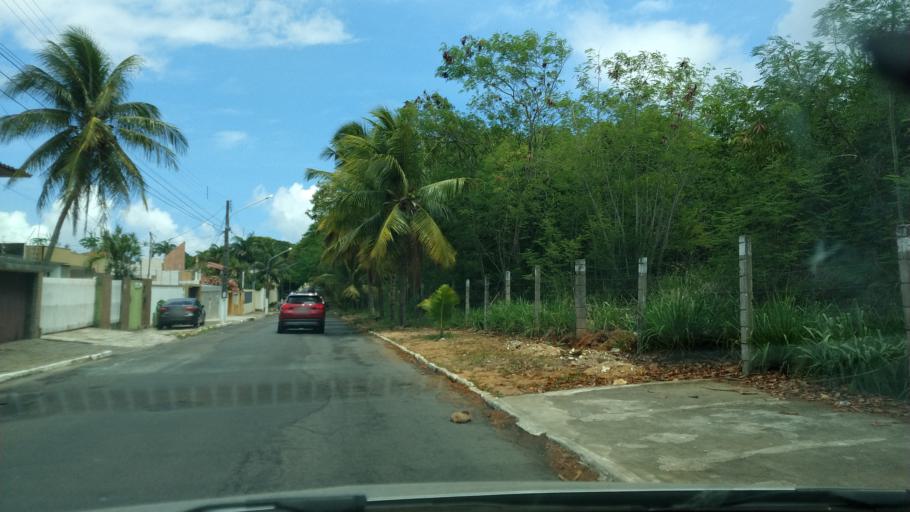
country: BR
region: Rio Grande do Norte
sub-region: Natal
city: Natal
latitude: -5.8484
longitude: -35.1976
